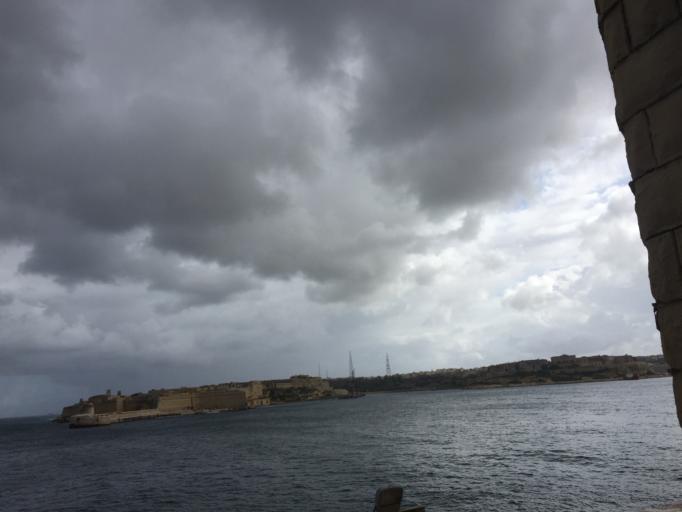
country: MT
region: Il-Belt Valletta
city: Valletta
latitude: 35.9003
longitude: 14.5191
